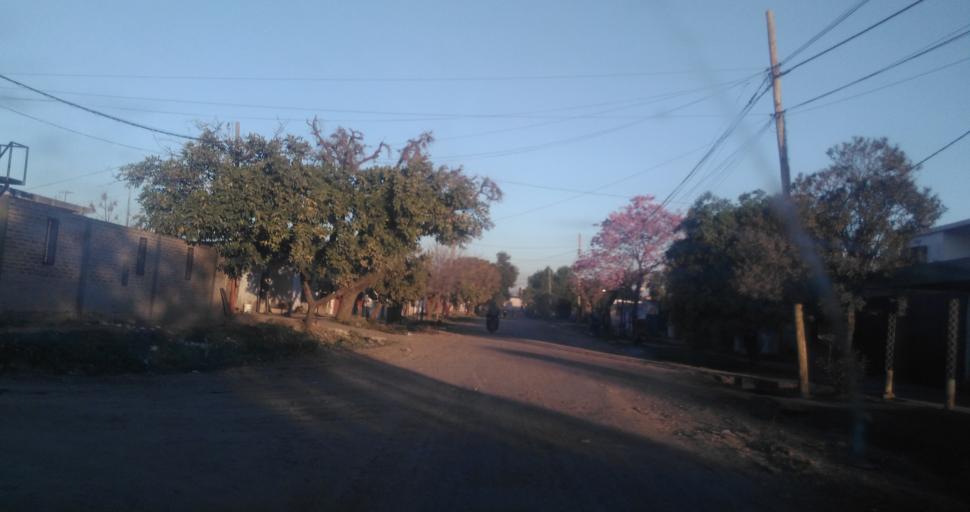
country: AR
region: Chaco
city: Fontana
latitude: -27.4287
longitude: -59.0080
